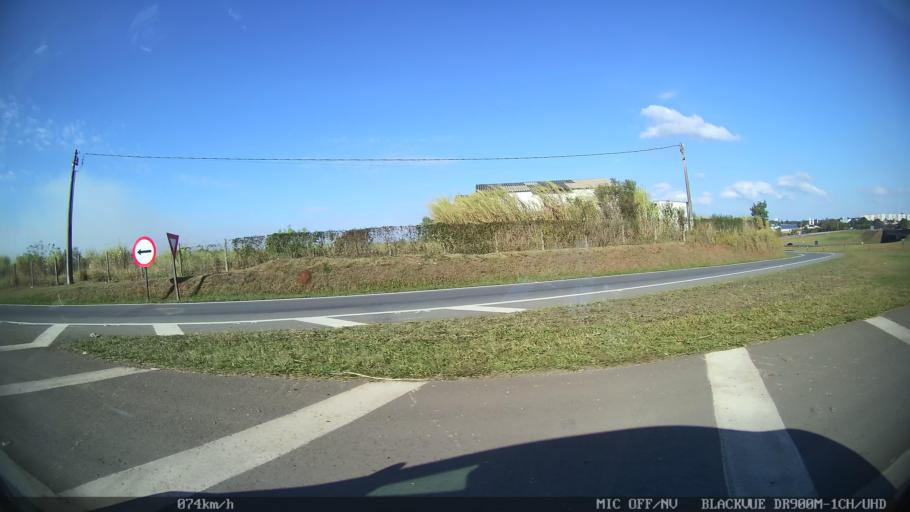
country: BR
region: Sao Paulo
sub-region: Piracicaba
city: Piracicaba
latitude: -22.7198
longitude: -47.6067
